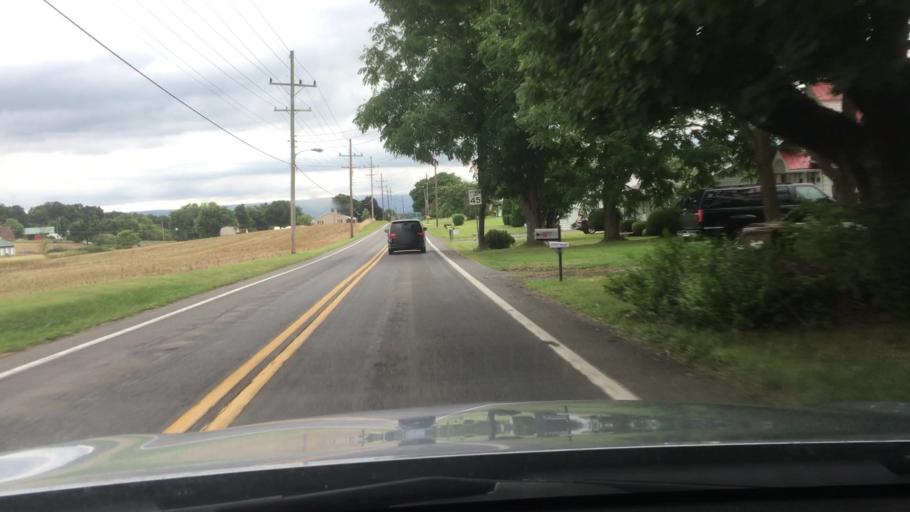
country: US
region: Pennsylvania
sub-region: Franklin County
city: Greencastle
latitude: 39.8637
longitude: -77.7631
